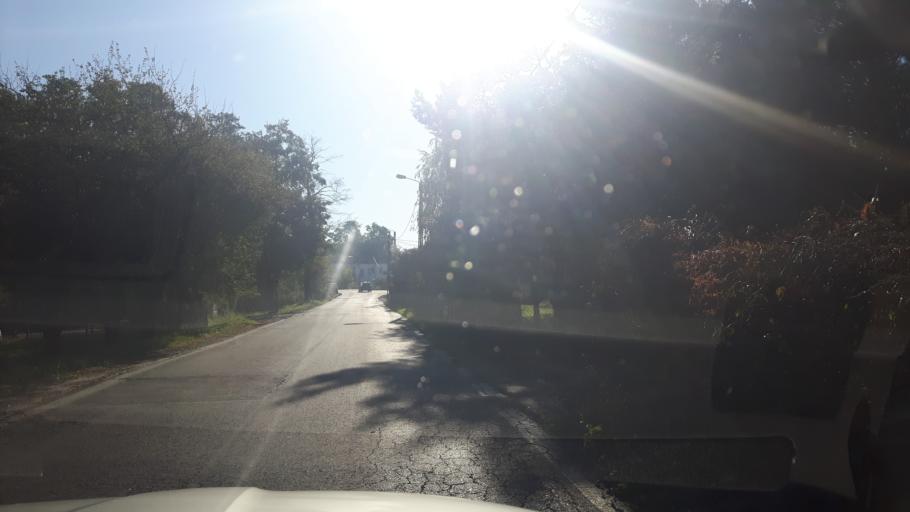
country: PL
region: Masovian Voivodeship
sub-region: Powiat legionowski
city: Stanislawow Pierwszy
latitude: 52.3499
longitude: 21.0269
